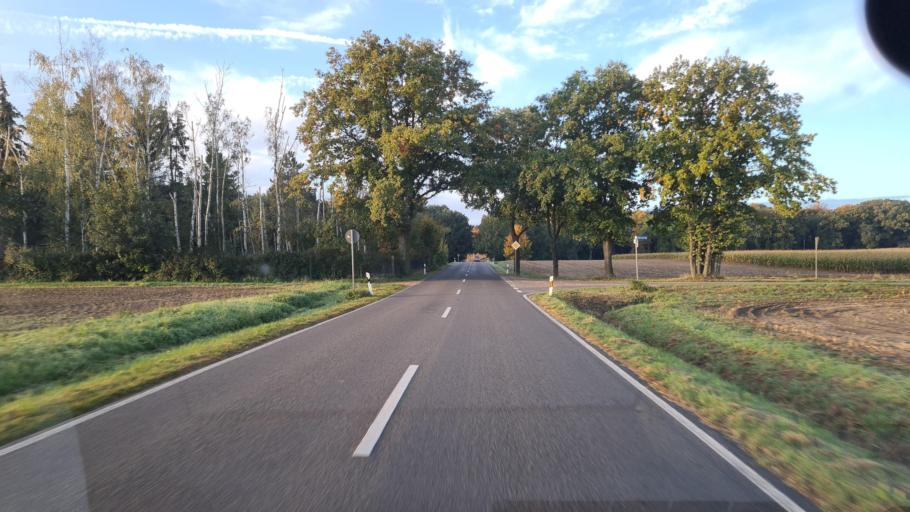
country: DE
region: Saxony
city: Machern
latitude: 51.3731
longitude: 12.6445
